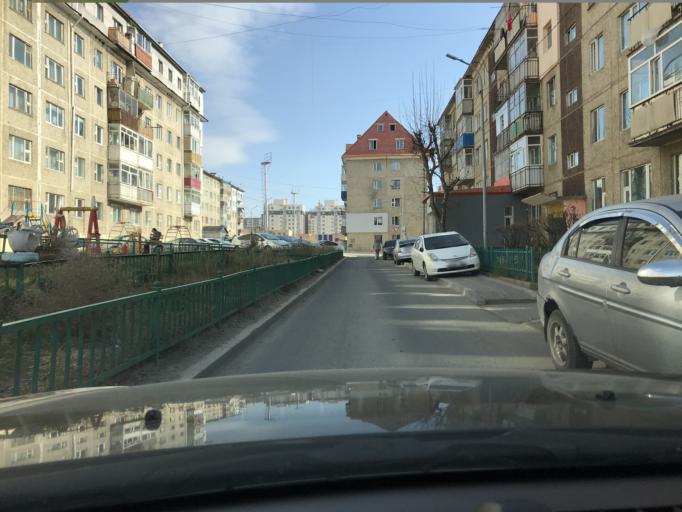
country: MN
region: Ulaanbaatar
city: Ulaanbaatar
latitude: 47.9224
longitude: 106.9464
